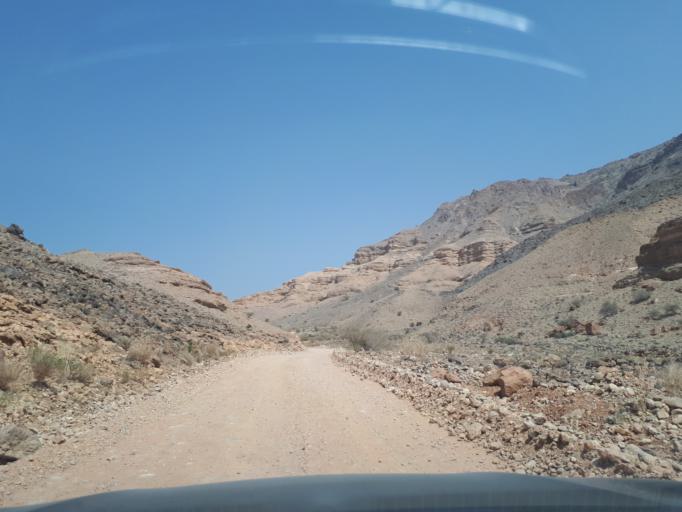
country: OM
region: Ash Sharqiyah
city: Ibra'
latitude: 23.0751
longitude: 58.8790
